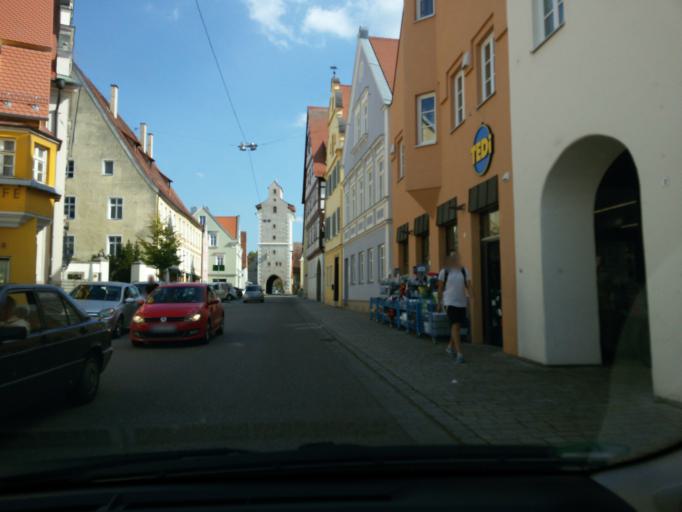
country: DE
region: Bavaria
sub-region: Swabia
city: Noerdlingen
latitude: 48.8493
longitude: 10.4903
